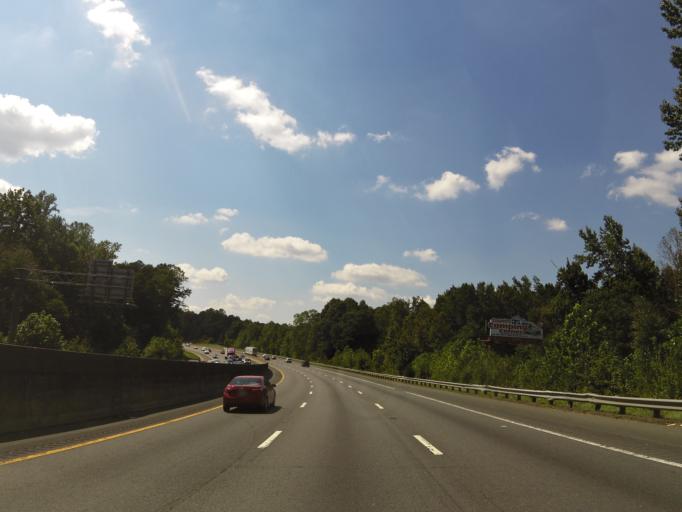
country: US
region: North Carolina
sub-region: Gaston County
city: Gastonia
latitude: 35.2839
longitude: -81.1724
